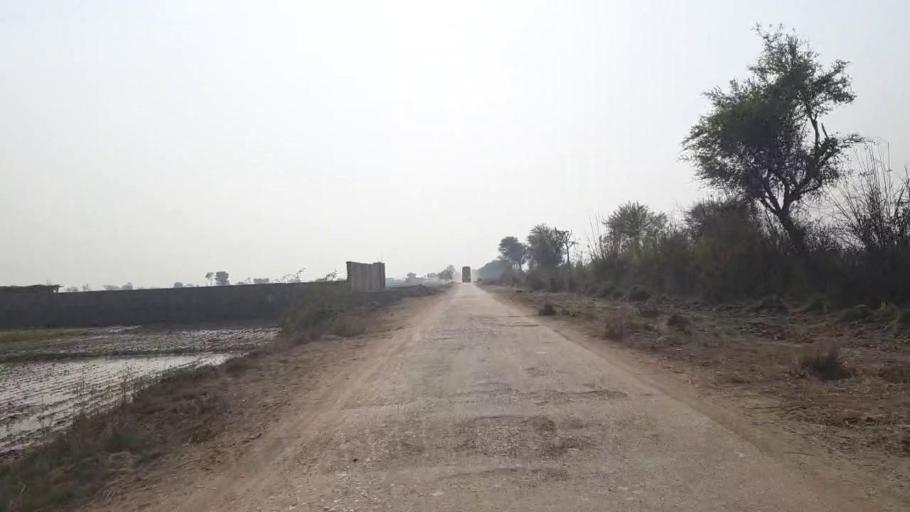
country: PK
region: Sindh
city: Hala
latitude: 25.9146
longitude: 68.4461
